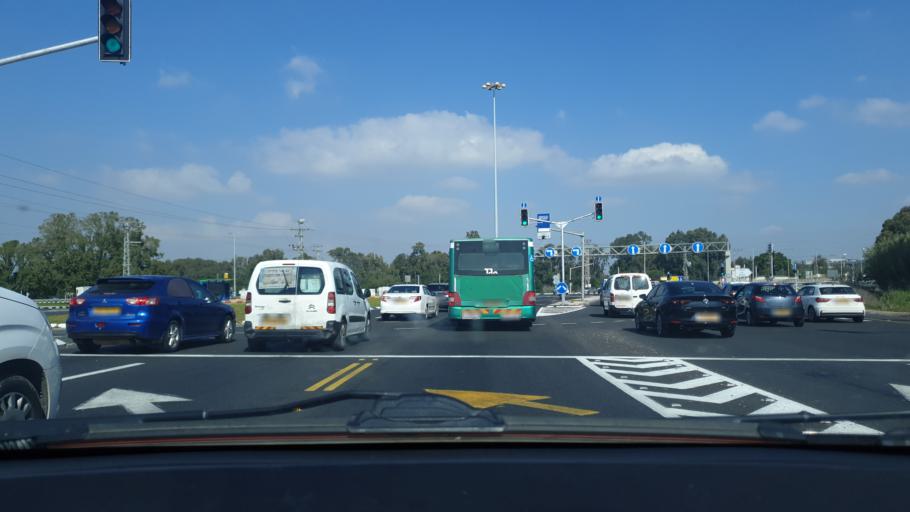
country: IL
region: Central District
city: Bet Dagan
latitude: 32.0004
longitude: 34.8202
